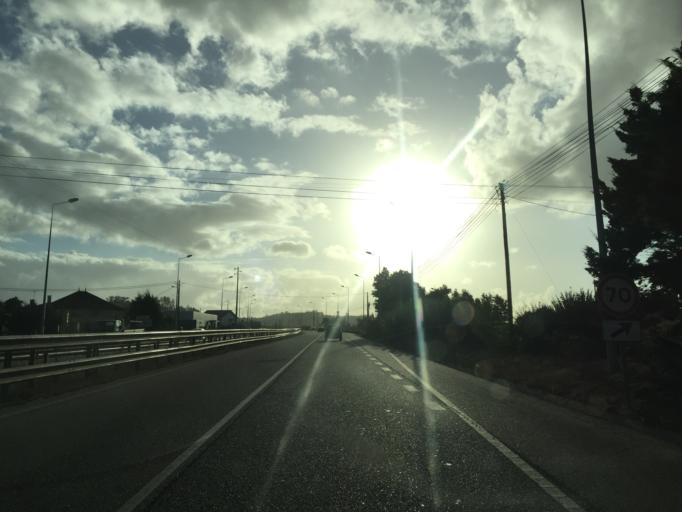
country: PT
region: Coimbra
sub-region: Coimbra
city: Coimbra
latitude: 40.2068
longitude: -8.4731
